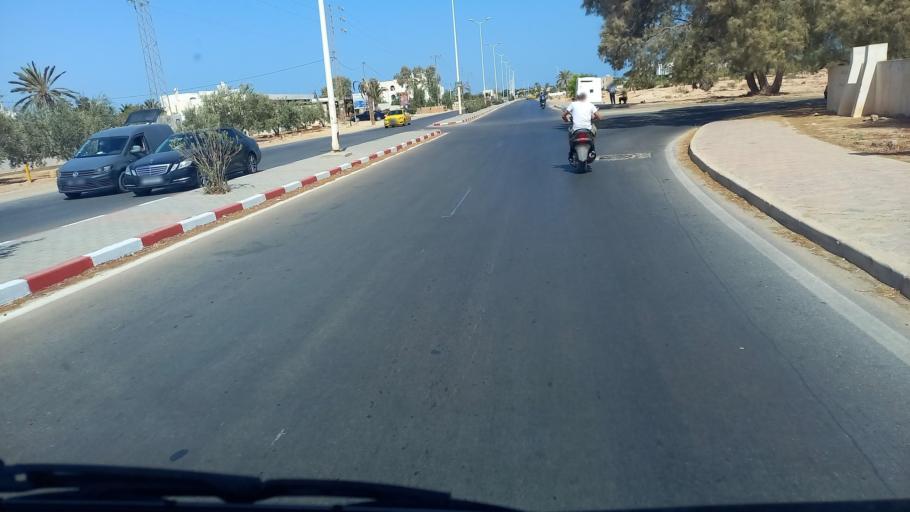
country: TN
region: Madanin
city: Midoun
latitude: 33.8543
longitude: 10.9795
